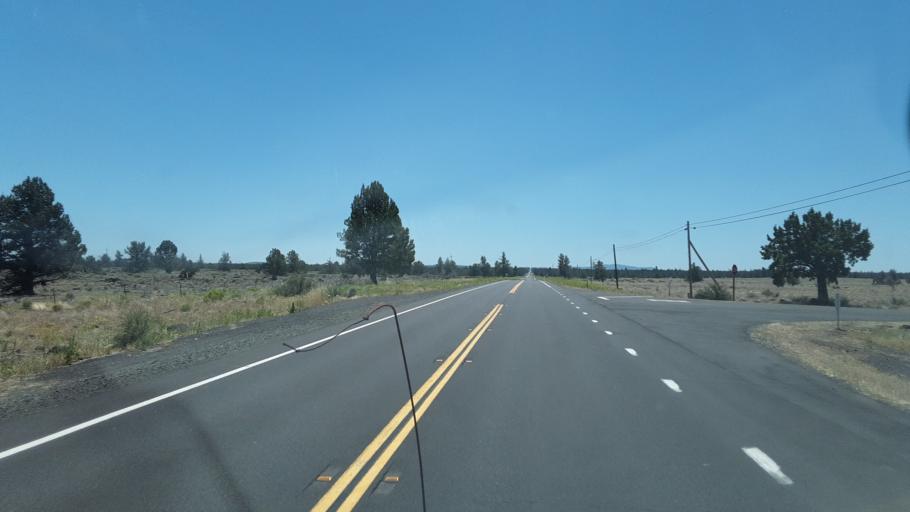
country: US
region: California
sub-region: Siskiyou County
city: Tulelake
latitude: 41.6794
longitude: -121.2637
